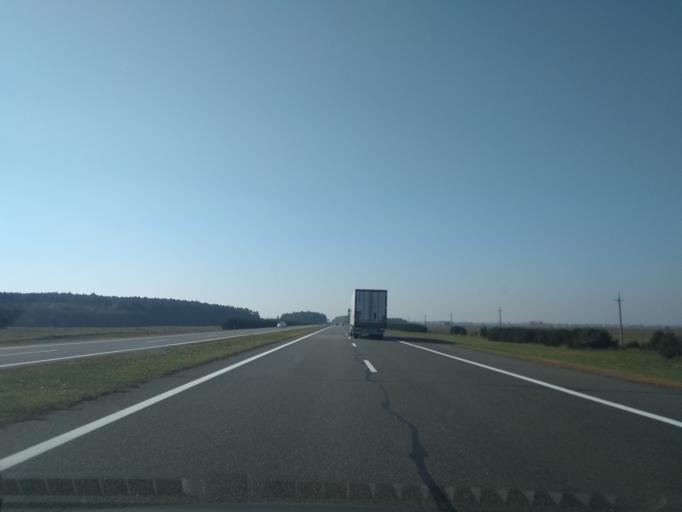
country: BY
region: Brest
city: Ivatsevichy
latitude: 52.7156
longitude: 25.4079
